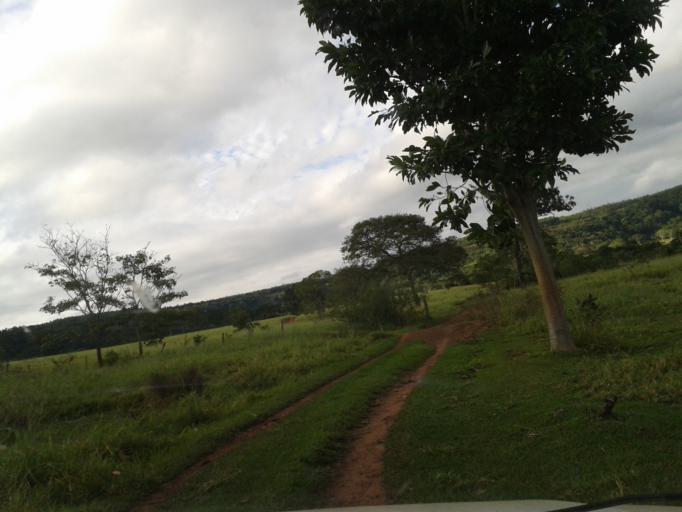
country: BR
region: Minas Gerais
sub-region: Campina Verde
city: Campina Verde
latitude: -19.4621
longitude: -49.6327
